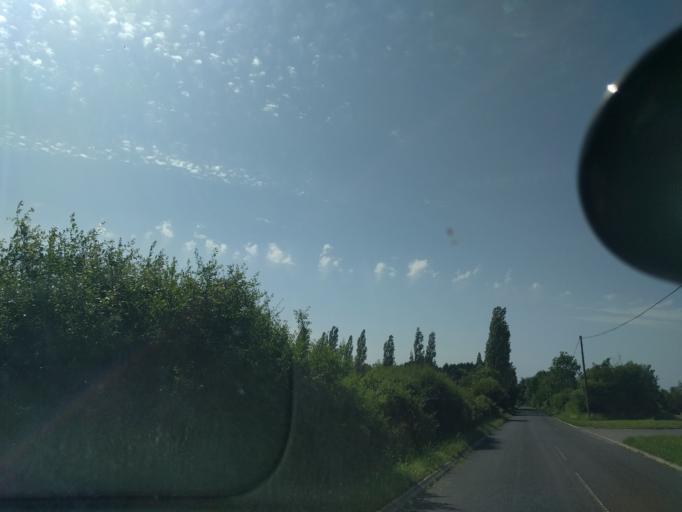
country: GB
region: England
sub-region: Wiltshire
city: Lyneham
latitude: 51.5328
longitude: -2.0005
